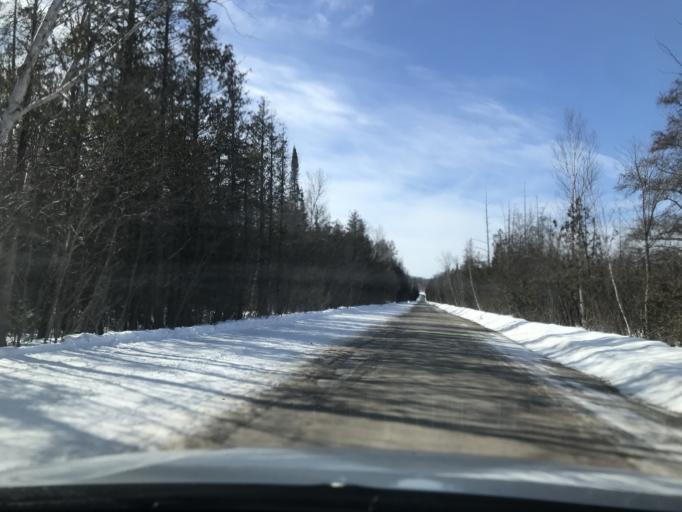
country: US
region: Wisconsin
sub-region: Marinette County
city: Peshtigo
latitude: 45.3007
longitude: -87.8247
